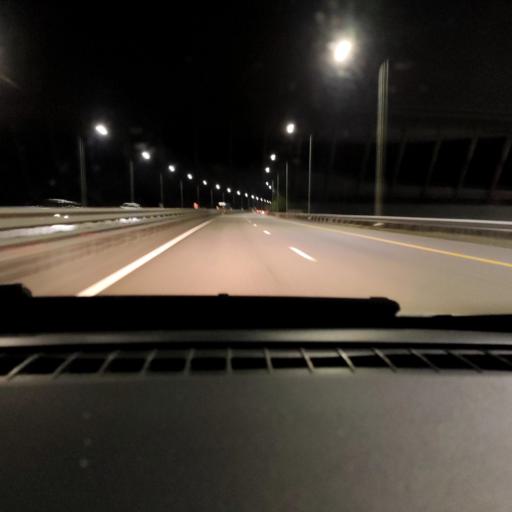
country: RU
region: Voronezj
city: Novaya Usman'
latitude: 51.6329
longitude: 39.3176
